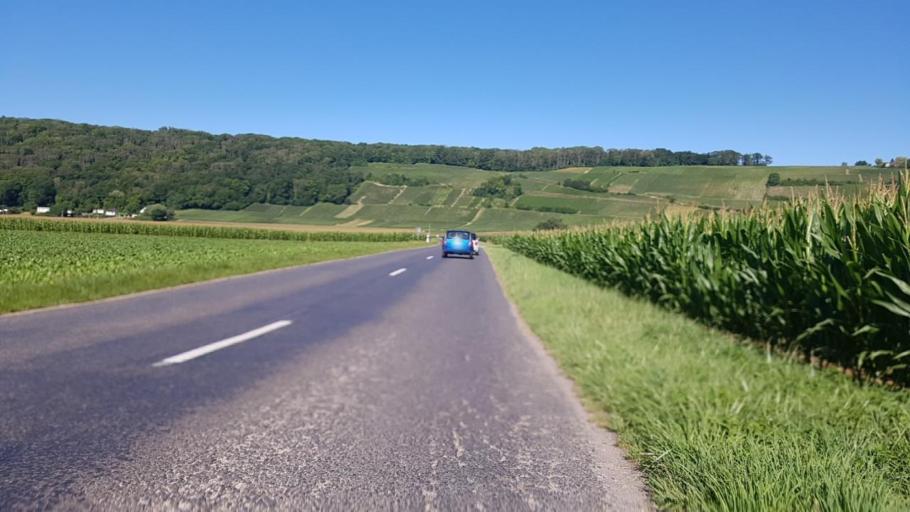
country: FR
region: Picardie
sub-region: Departement de l'Aisne
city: Chezy-sur-Marne
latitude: 49.0028
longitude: 3.3522
